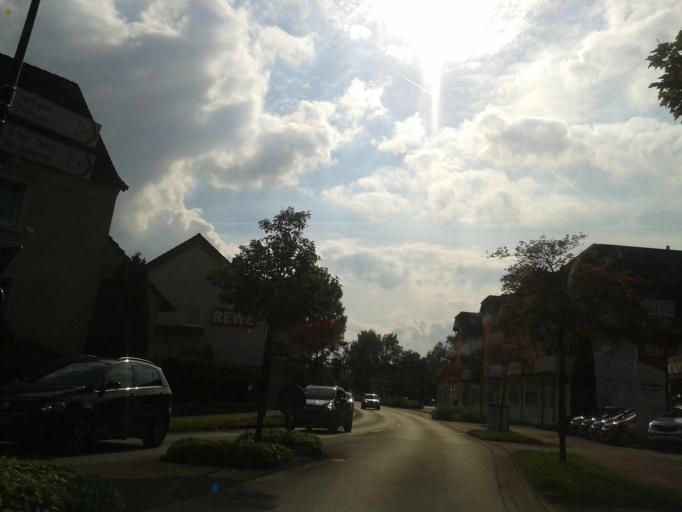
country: DE
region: North Rhine-Westphalia
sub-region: Regierungsbezirk Detmold
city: Schlangen
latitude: 51.8108
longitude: 8.8452
